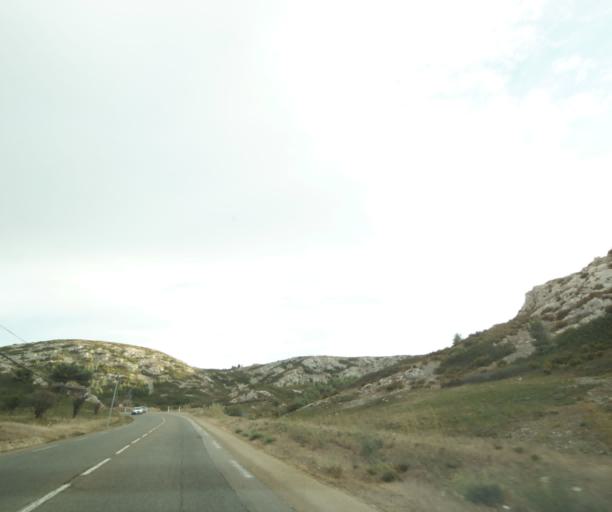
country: FR
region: Provence-Alpes-Cote d'Azur
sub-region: Departement des Bouches-du-Rhone
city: Le Rove
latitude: 43.3677
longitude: 5.2339
